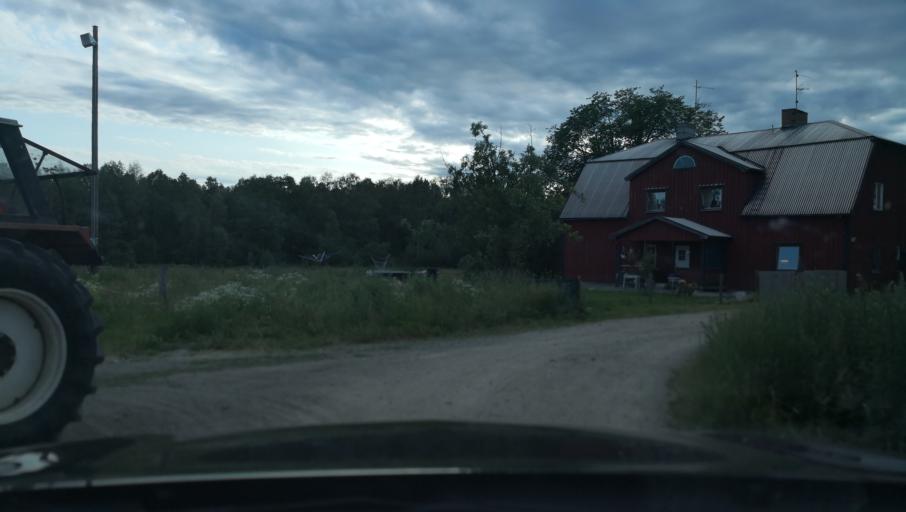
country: SE
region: Dalarna
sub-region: Ludvika Kommun
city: Ludvika
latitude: 60.0750
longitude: 15.2599
